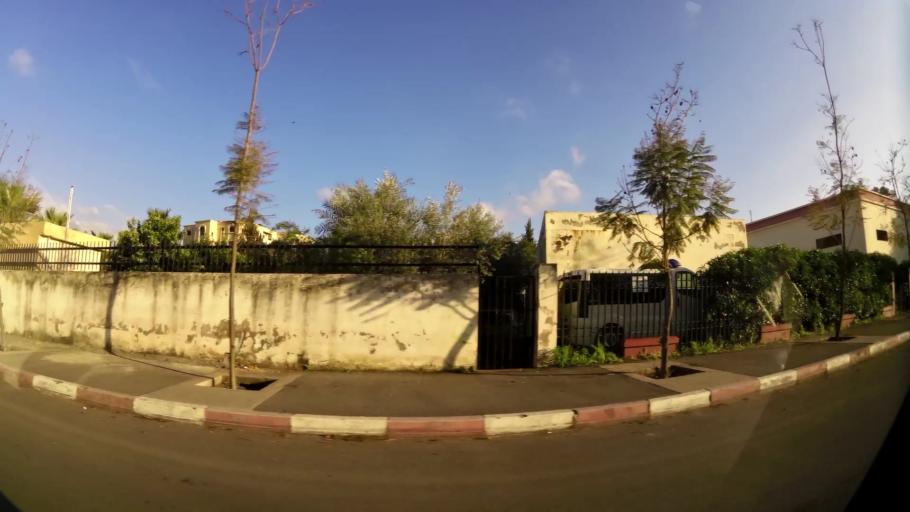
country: MA
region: Chaouia-Ouardigha
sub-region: Settat Province
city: Settat
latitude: 33.0111
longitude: -7.6163
